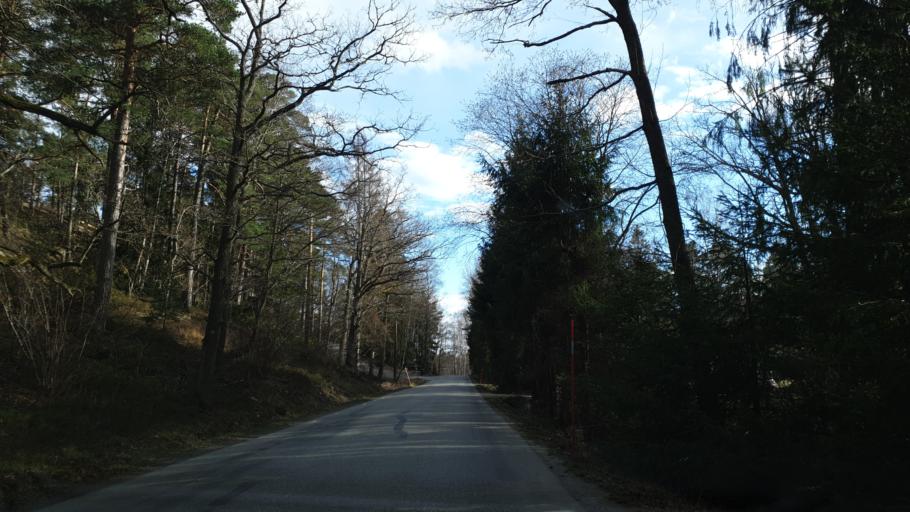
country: SE
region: Stockholm
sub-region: Varmdo Kommun
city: Holo
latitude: 59.3619
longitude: 18.6703
